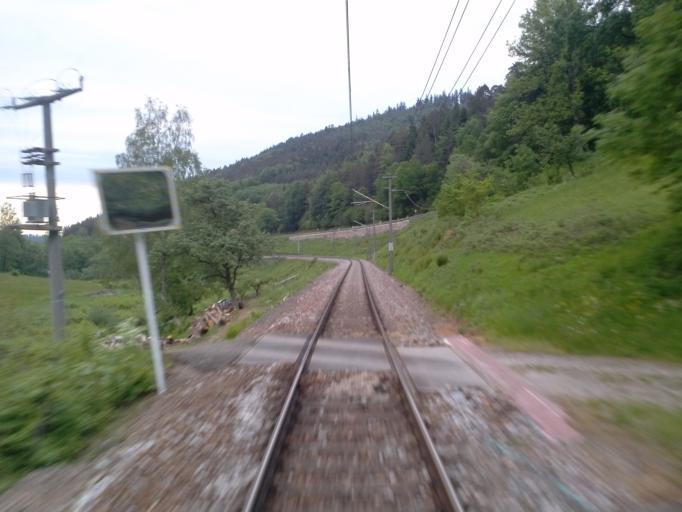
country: DE
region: Baden-Wuerttemberg
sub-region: Karlsruhe Region
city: Bad Herrenalb
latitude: 48.8162
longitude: 8.4449
